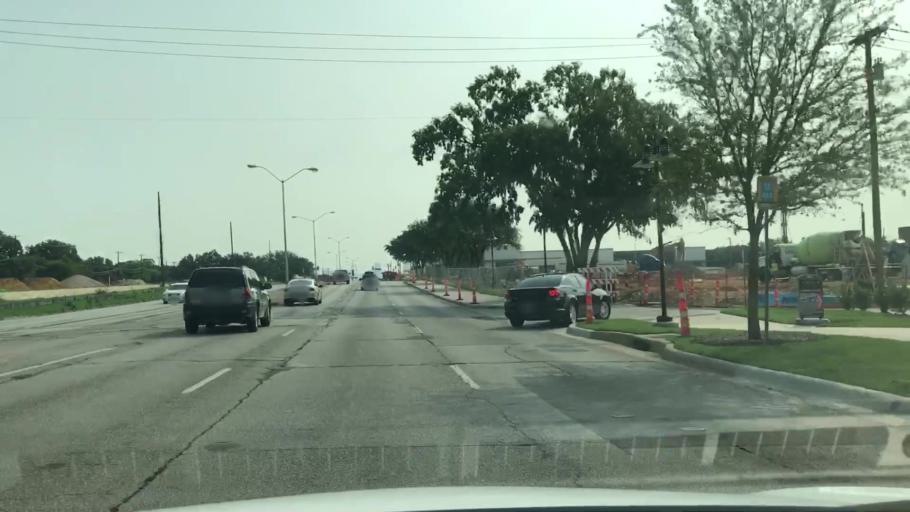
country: US
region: Texas
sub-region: Dallas County
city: Cockrell Hill
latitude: 32.7598
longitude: -96.8613
